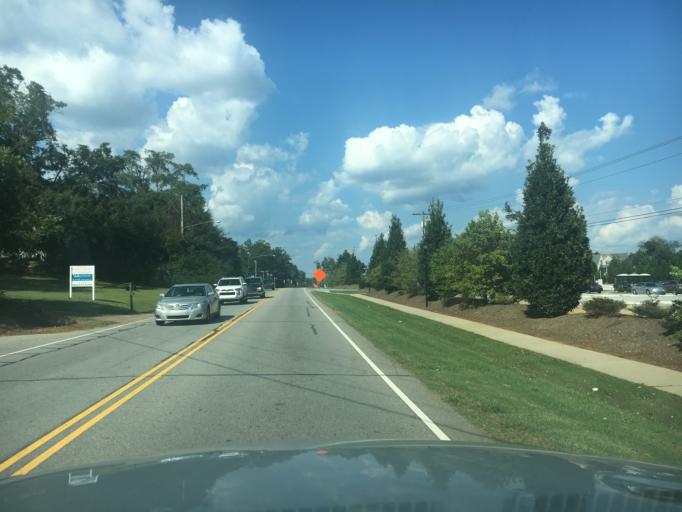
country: US
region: South Carolina
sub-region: Anderson County
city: Pendleton
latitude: 34.6357
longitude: -82.7833
